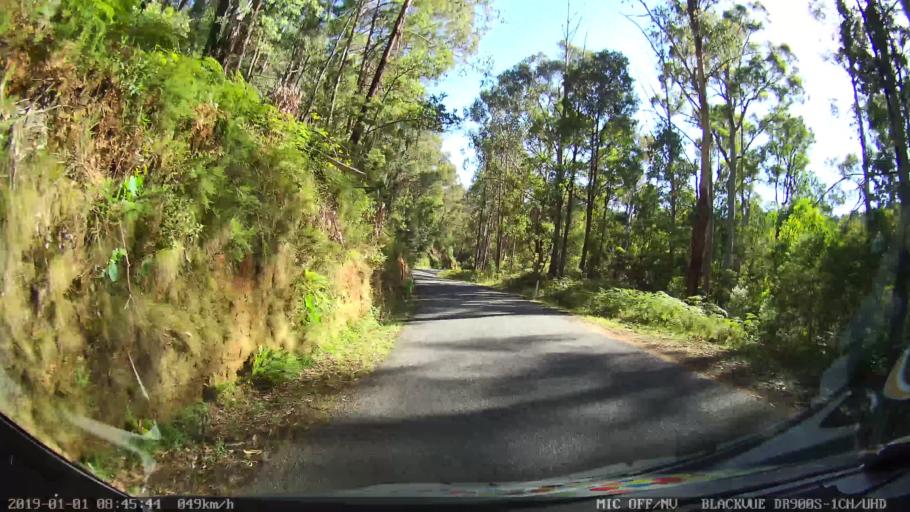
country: AU
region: New South Wales
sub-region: Snowy River
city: Jindabyne
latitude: -36.3037
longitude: 148.1899
